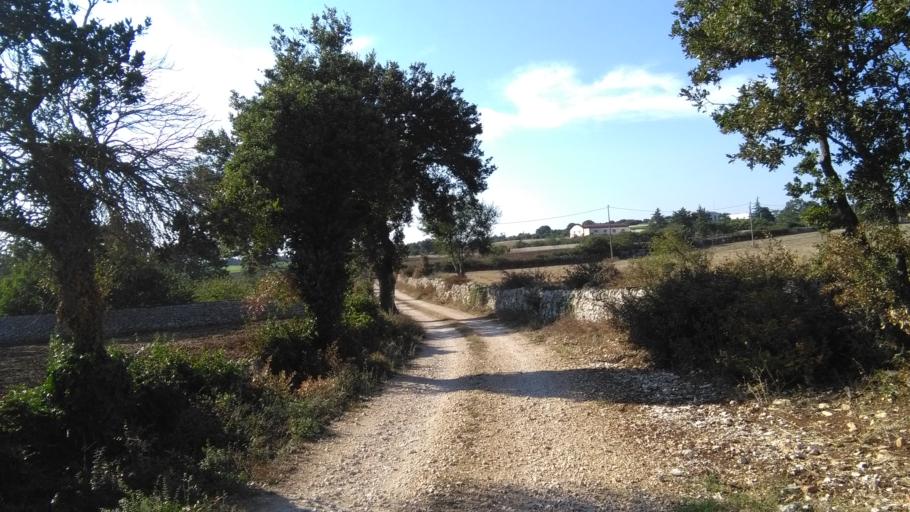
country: IT
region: Apulia
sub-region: Provincia di Bari
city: Putignano
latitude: 40.8213
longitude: 17.0572
